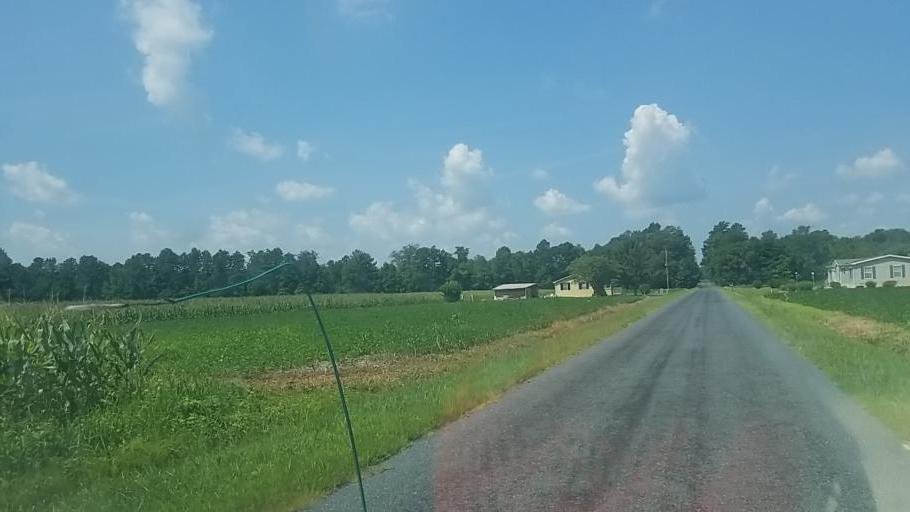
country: US
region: Maryland
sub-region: Worcester County
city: Berlin
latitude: 38.2976
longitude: -75.2829
